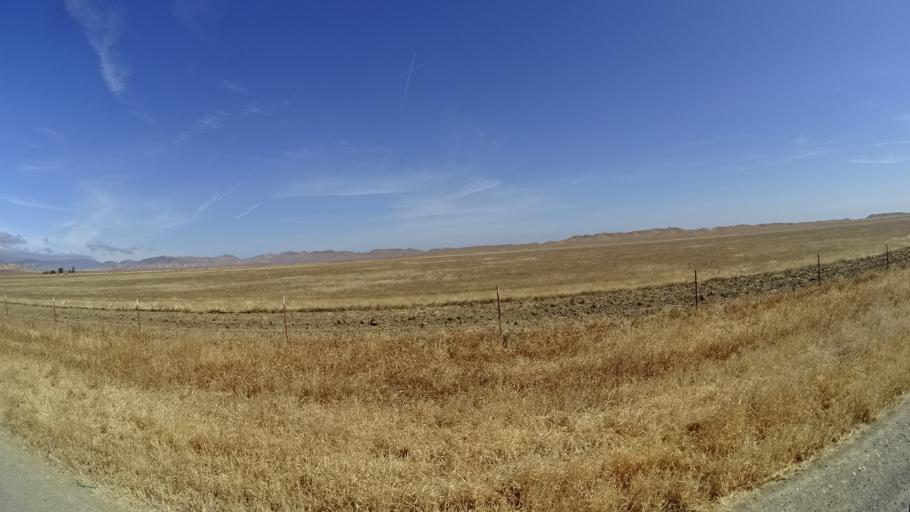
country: US
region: California
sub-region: Kings County
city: Avenal
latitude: 35.8178
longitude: -120.0905
